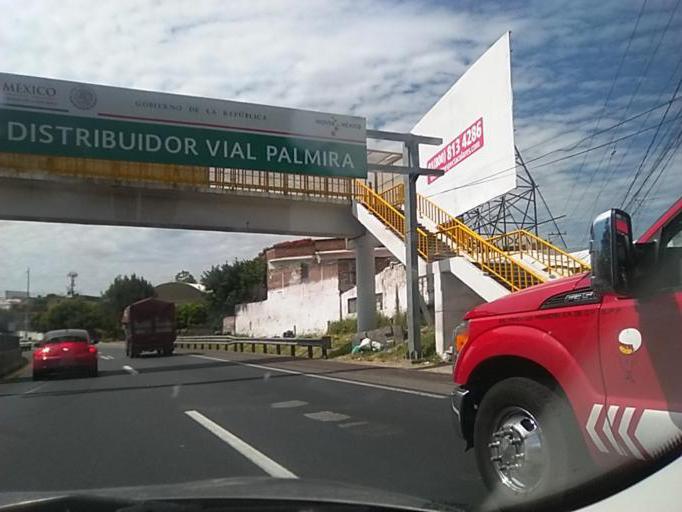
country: MX
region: Morelos
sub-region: Cuernavaca
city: Cuernavaca
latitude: 18.8967
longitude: -99.2264
